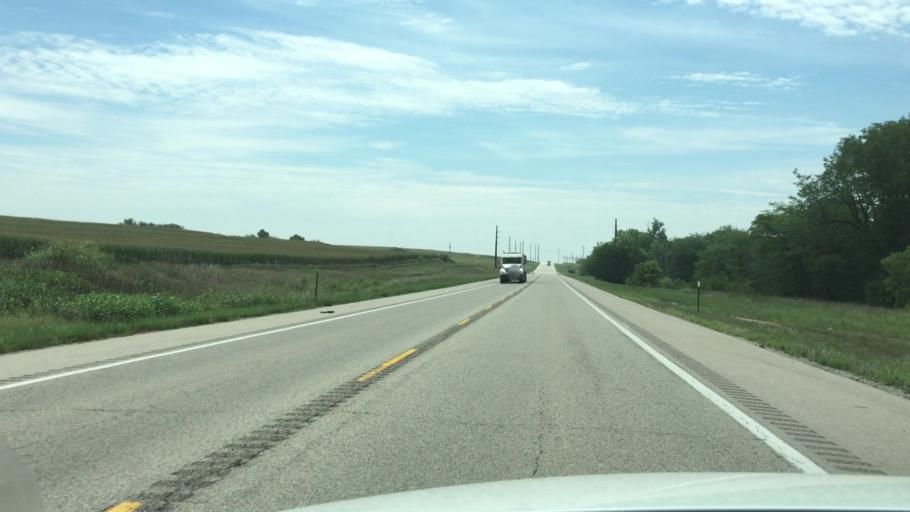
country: US
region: Kansas
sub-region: Nemaha County
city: Sabetha
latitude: 39.8305
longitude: -95.7325
